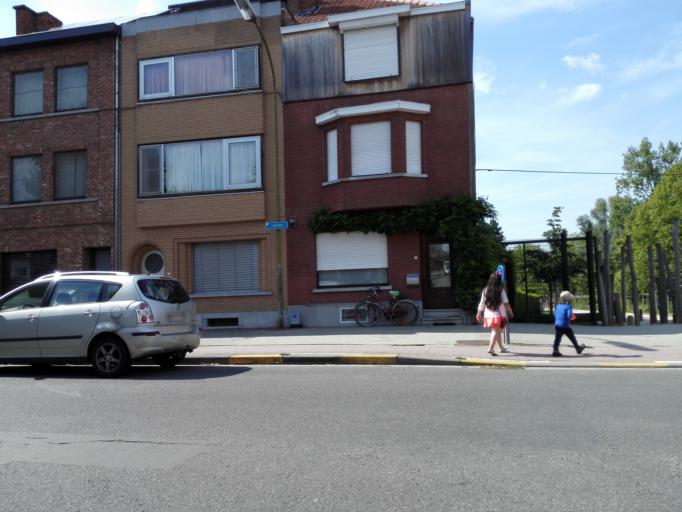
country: BE
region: Flanders
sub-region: Provincie Vlaams-Brabant
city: Leuven
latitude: 50.8902
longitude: 4.7217
